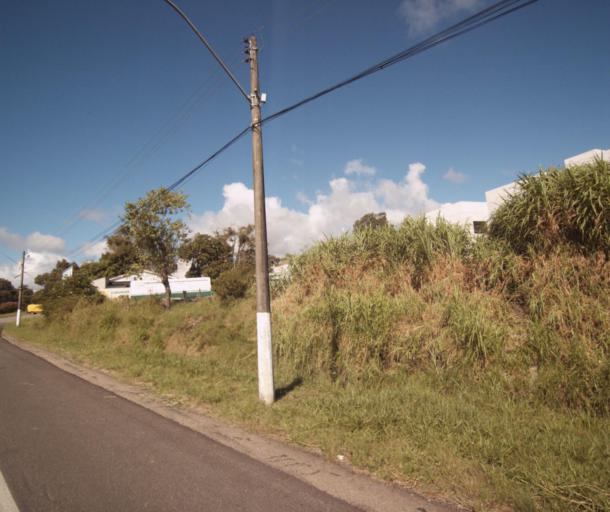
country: BR
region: Rio Grande do Sul
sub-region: Pelotas
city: Pelotas
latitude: -31.7624
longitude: -52.3563
